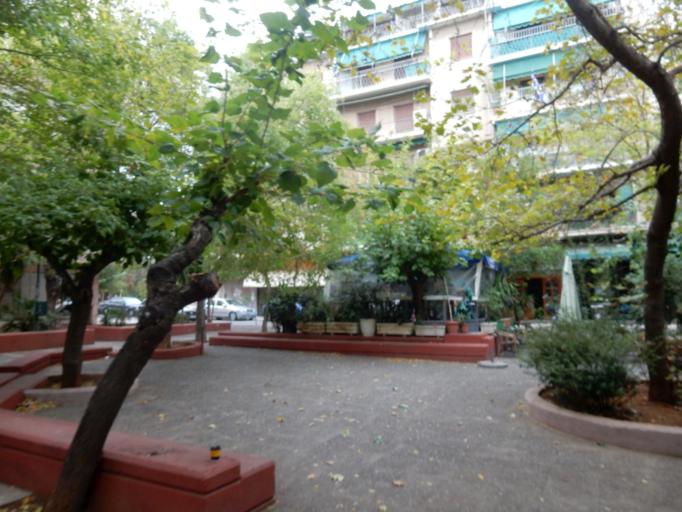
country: GR
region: Attica
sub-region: Nomarchia Athinas
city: Kipseli
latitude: 38.0127
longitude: 23.7314
